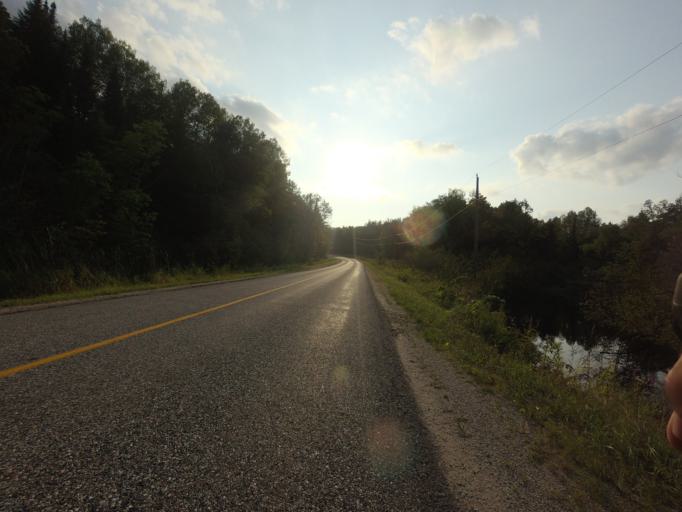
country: CA
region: Ontario
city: Perth
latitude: 44.9671
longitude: -76.7009
